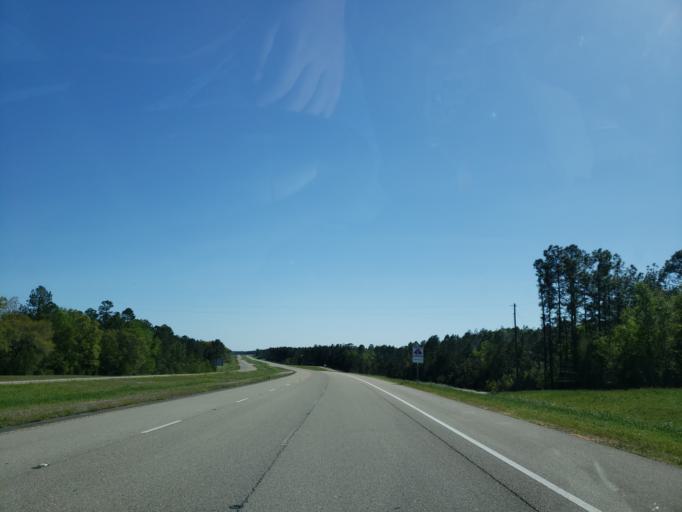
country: US
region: Mississippi
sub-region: Harrison County
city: Lyman
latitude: 30.5488
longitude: -89.0288
